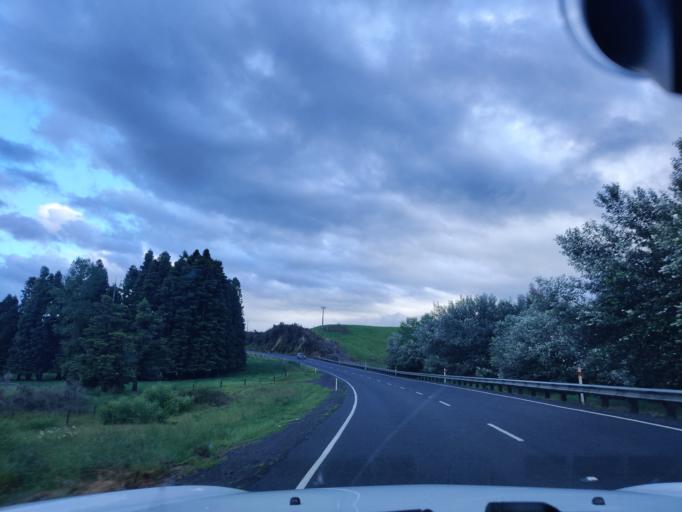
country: NZ
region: Waikato
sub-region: South Waikato District
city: Tokoroa
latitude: -38.3744
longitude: 175.7939
